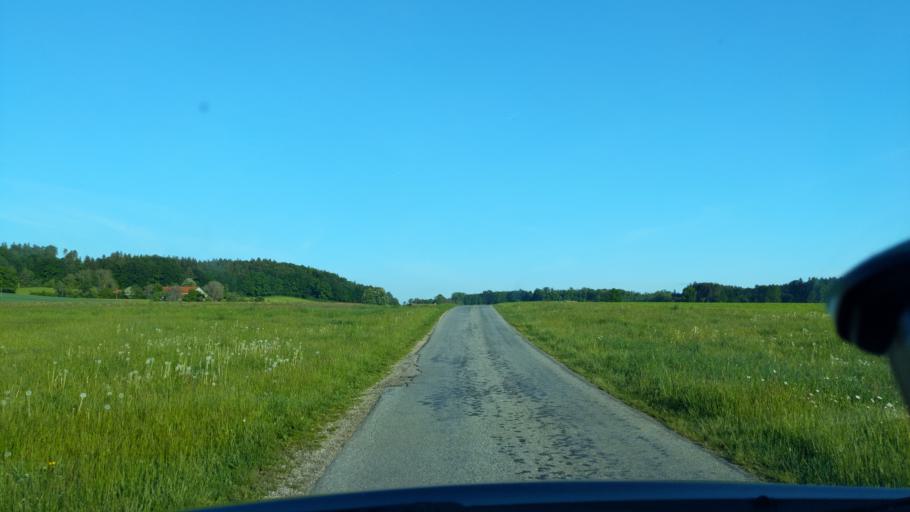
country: DE
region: Bavaria
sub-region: Upper Bavaria
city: Ebersberg
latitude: 48.0611
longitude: 11.9754
